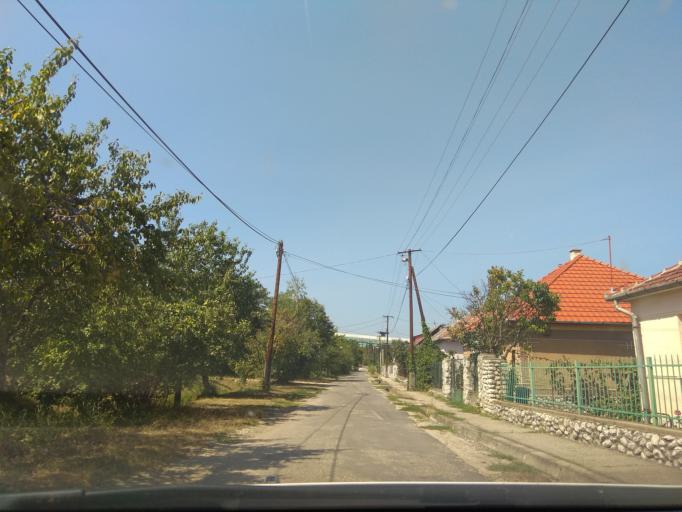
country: HU
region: Borsod-Abauj-Zemplen
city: Miskolc
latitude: 48.0643
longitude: 20.7797
